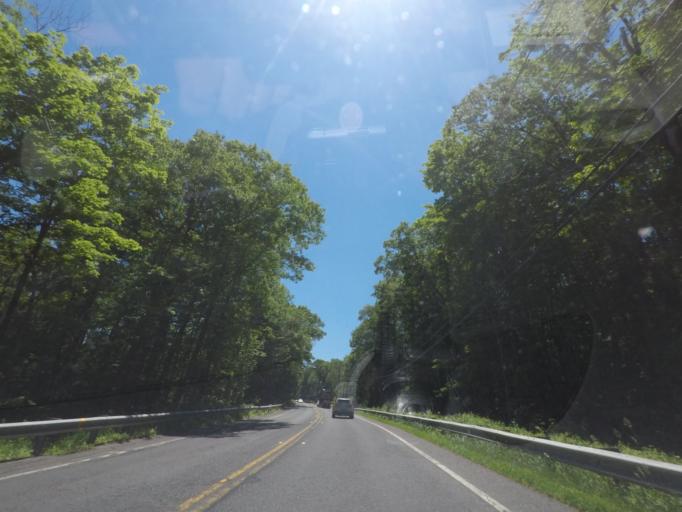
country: US
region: Massachusetts
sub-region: Berkshire County
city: Becket
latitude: 42.2757
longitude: -73.1421
